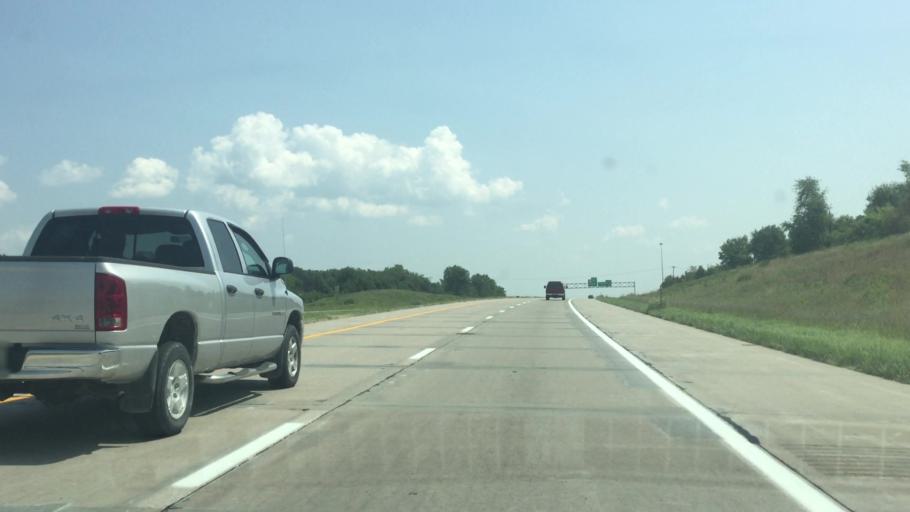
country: US
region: Kansas
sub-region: Franklin County
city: Ottawa
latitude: 38.5685
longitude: -95.2954
